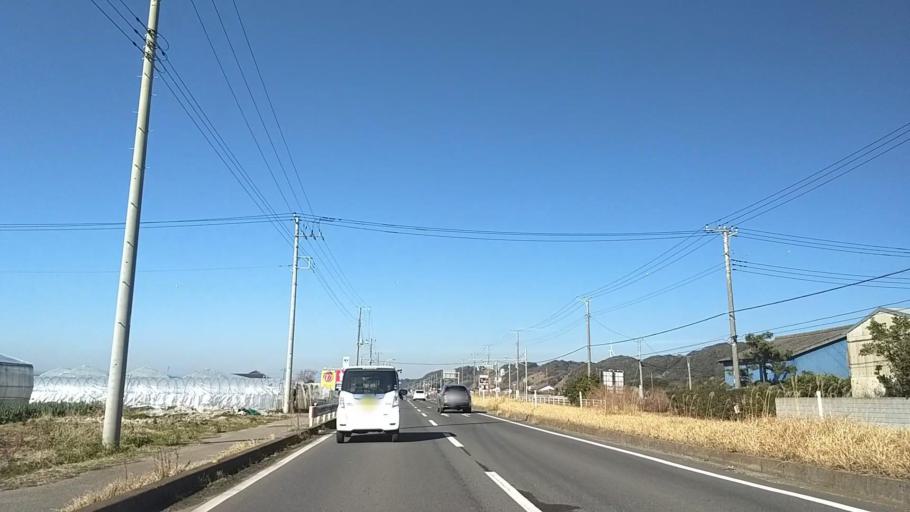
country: JP
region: Chiba
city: Asahi
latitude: 35.7025
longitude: 140.7289
